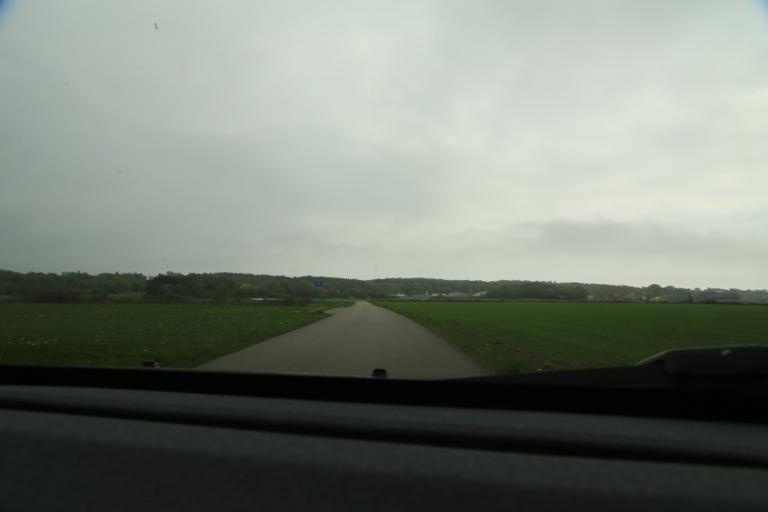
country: SE
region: Halland
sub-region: Kungsbacka Kommun
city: Frillesas
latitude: 57.2310
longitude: 12.1559
